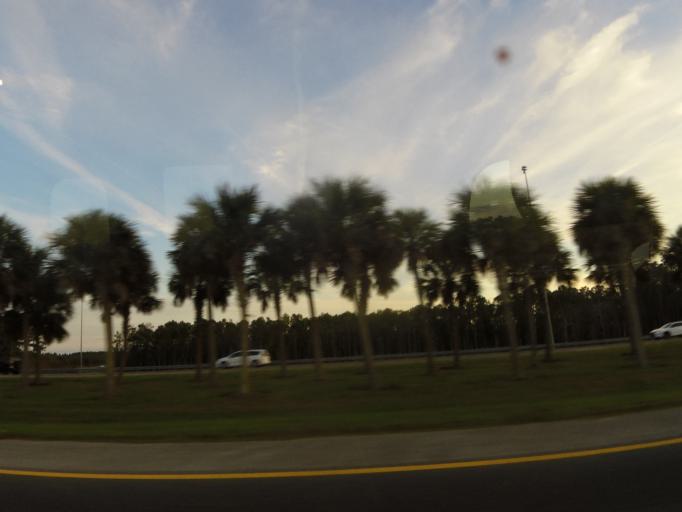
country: US
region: Florida
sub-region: Saint Johns County
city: Palm Valley
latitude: 30.1104
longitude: -81.4480
